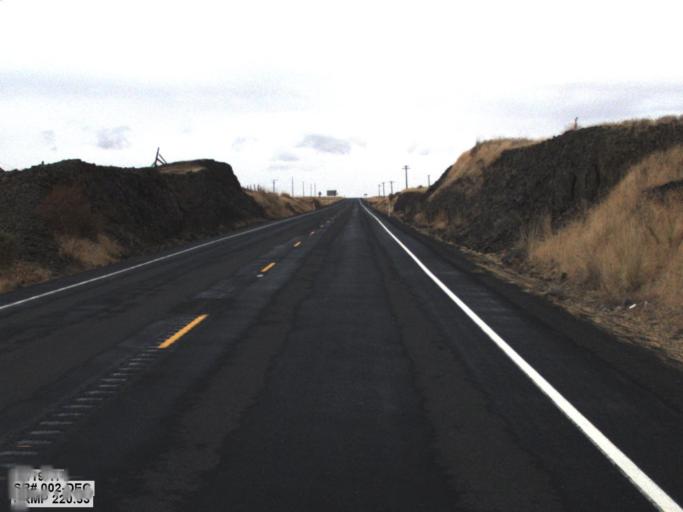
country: US
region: Washington
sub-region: Okanogan County
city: Coulee Dam
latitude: 47.7630
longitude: -118.7293
